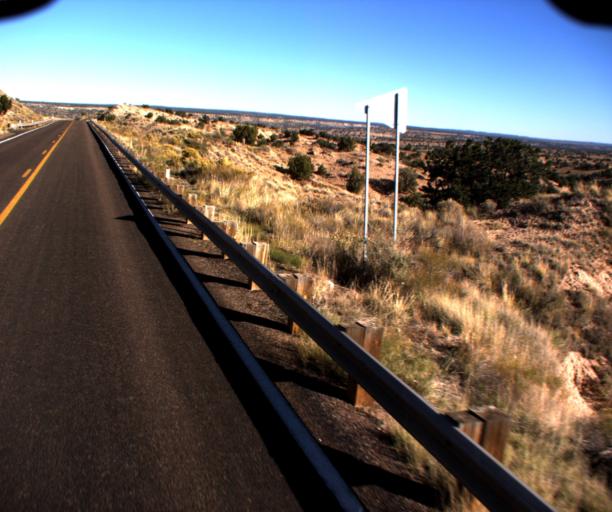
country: US
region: Arizona
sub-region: Navajo County
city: First Mesa
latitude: 35.7398
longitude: -110.1193
